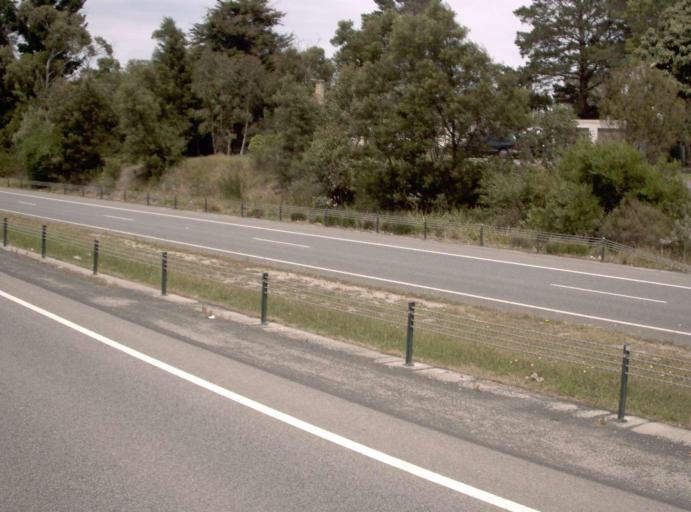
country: AU
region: Victoria
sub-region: Casey
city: Cranbourne South
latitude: -38.1374
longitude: 145.2277
